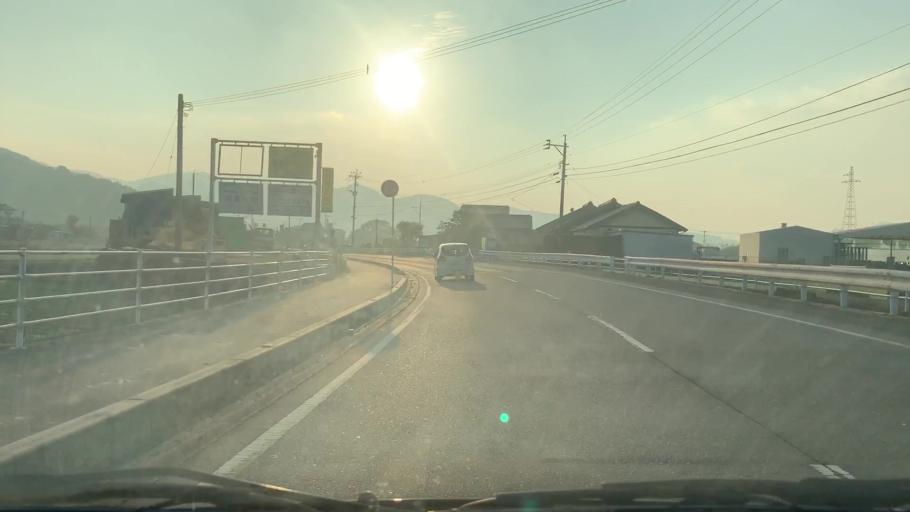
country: JP
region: Saga Prefecture
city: Saga-shi
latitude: 33.2780
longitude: 130.1488
